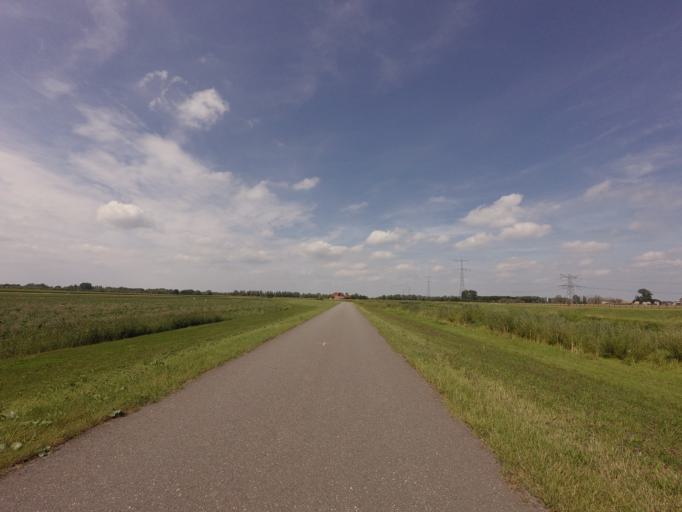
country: NL
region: South Holland
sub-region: Gemeente Sliedrecht
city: Sliedrecht
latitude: 51.7880
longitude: 4.8021
